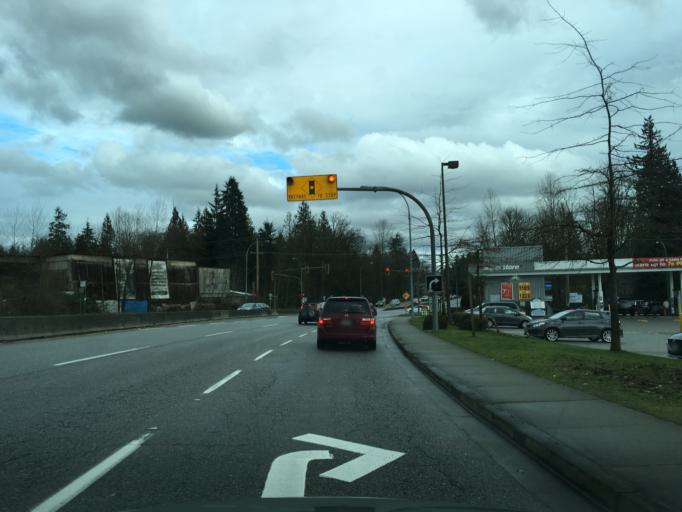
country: CA
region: British Columbia
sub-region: Fraser Valley Regional District
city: North Vancouver
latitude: 49.3121
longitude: -123.0227
